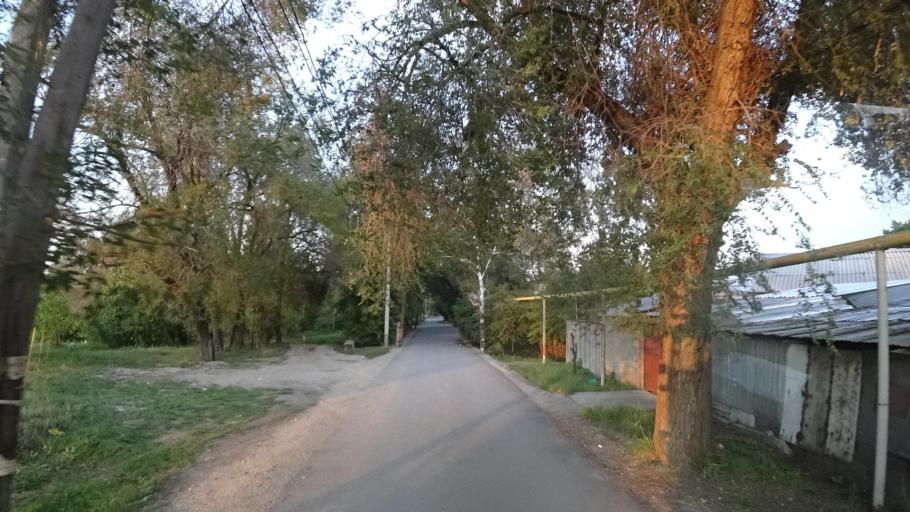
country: KZ
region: Almaty Oblysy
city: Pervomayskiy
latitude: 43.3383
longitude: 76.9943
